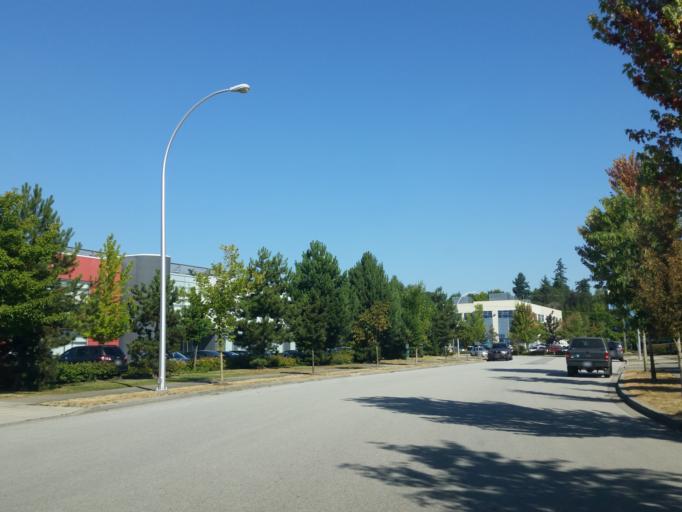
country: CA
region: British Columbia
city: Langley
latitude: 49.0977
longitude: -122.7085
